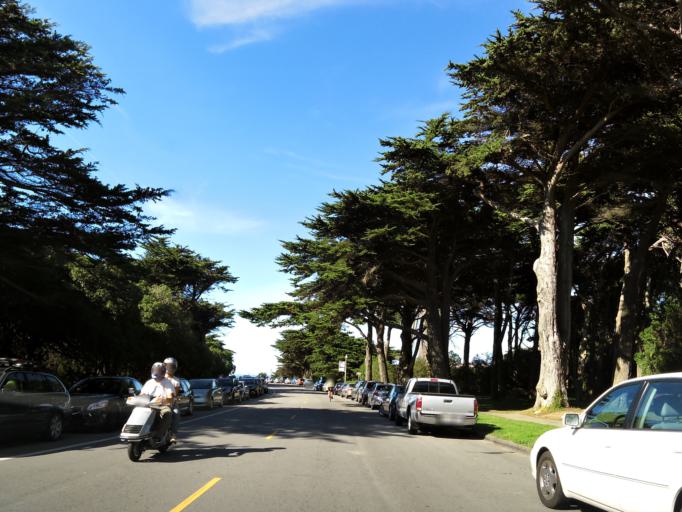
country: US
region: California
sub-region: San Mateo County
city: Daly City
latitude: 37.7694
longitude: -122.5085
